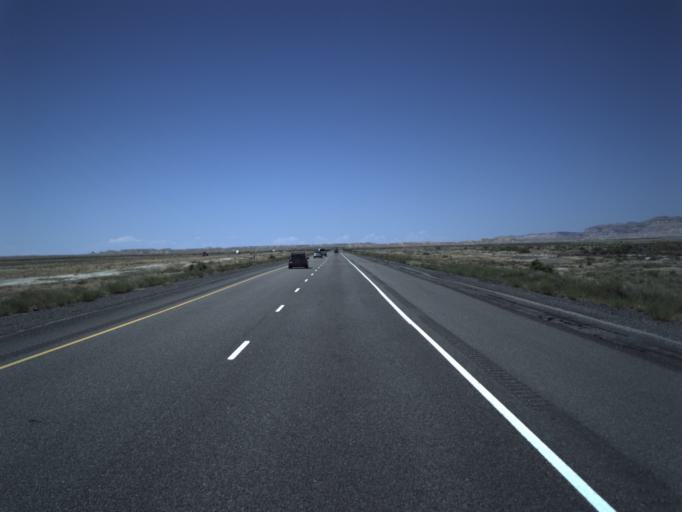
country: US
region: Utah
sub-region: Grand County
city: Moab
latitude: 38.9428
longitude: -109.5676
